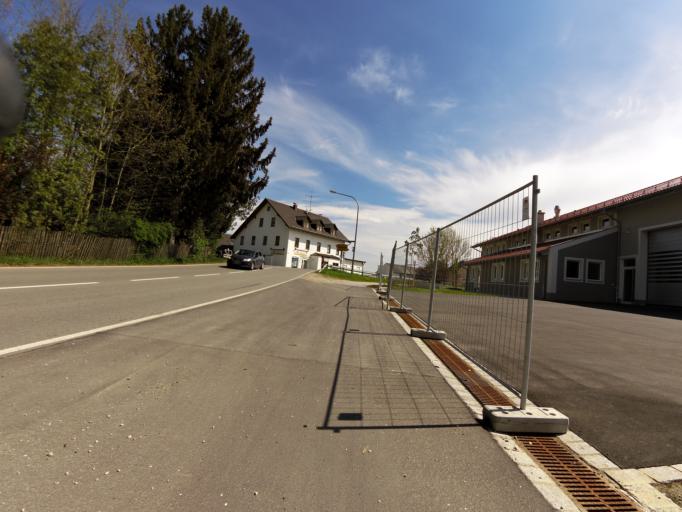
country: DE
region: Bavaria
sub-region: Lower Bavaria
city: Bruckberg
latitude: 48.5156
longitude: 11.9949
